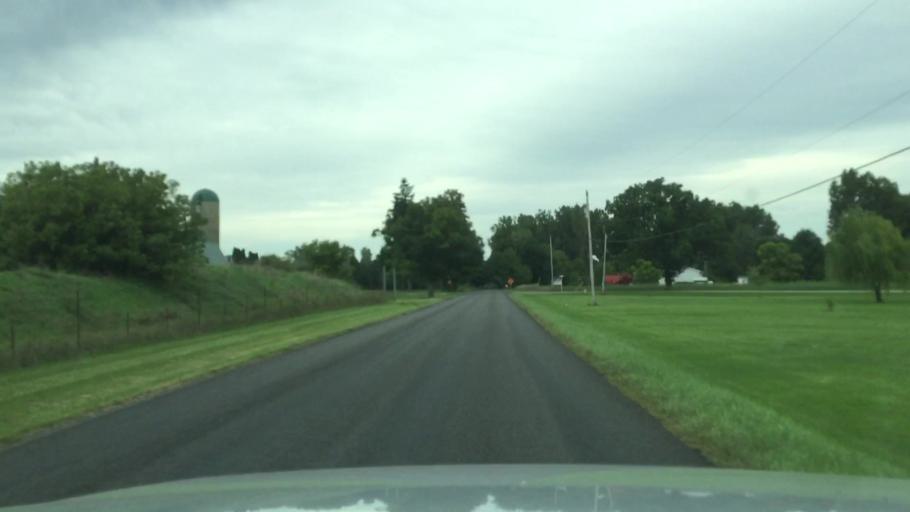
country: US
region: Michigan
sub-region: Shiawassee County
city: Durand
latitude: 42.8745
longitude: -84.0584
